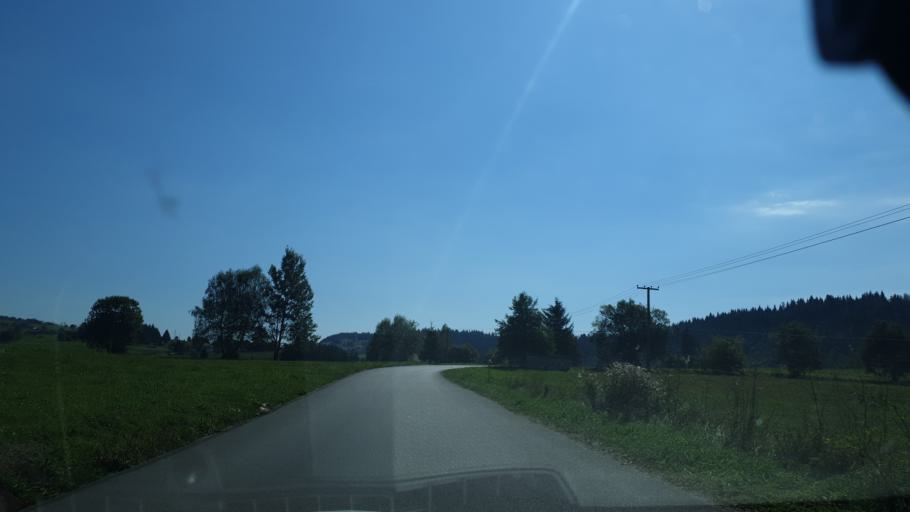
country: RS
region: Central Serbia
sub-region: Zlatiborski Okrug
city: Nova Varos
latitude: 43.4368
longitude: 19.8706
